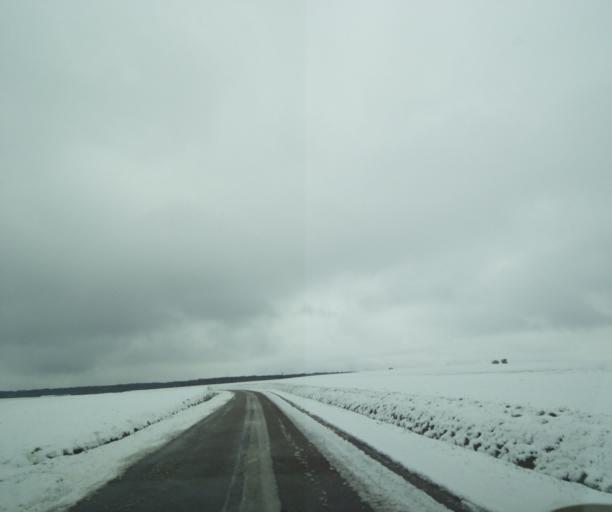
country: FR
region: Champagne-Ardenne
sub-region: Departement de la Haute-Marne
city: Laneuville-a-Remy
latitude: 48.4030
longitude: 4.8536
